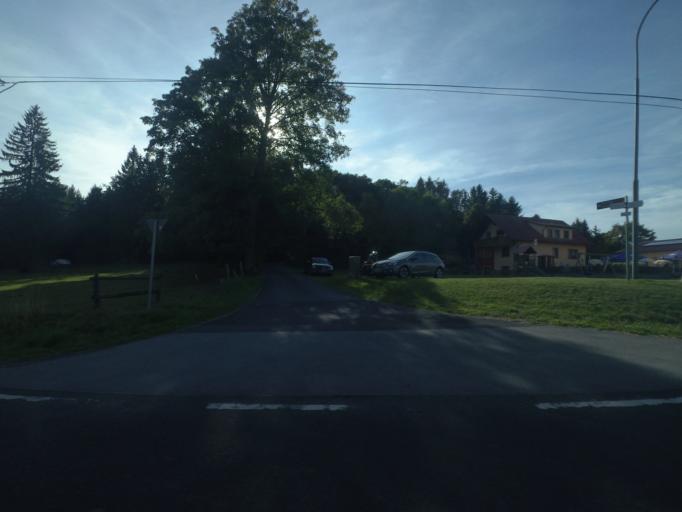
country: DE
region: Hesse
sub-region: Regierungsbezirk Kassel
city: Poppenhausen
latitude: 50.5239
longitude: 9.8665
